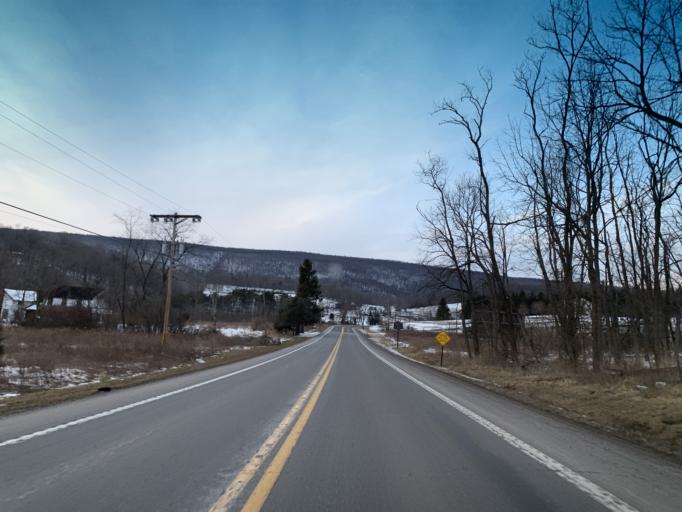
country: US
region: Maryland
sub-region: Allegany County
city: Cumberland
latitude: 39.7255
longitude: -78.7089
